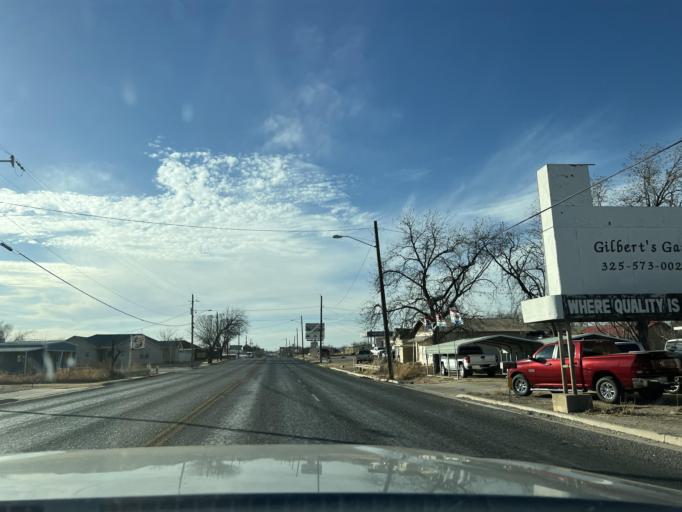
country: US
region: Texas
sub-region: Scurry County
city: Snyder
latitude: 32.7170
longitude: -100.9092
